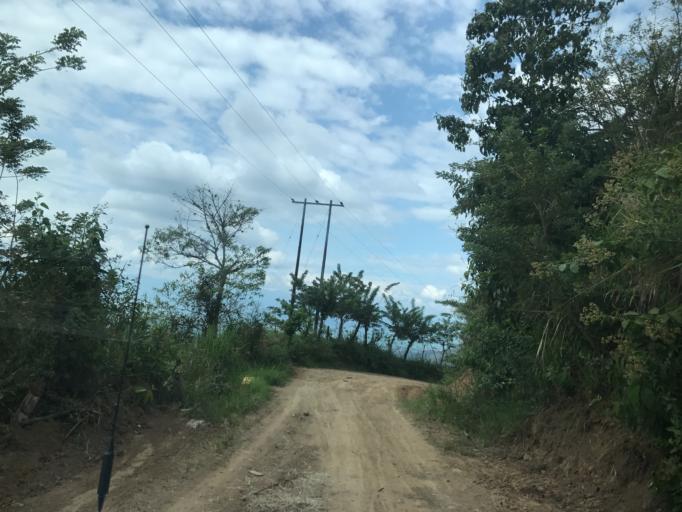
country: CO
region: Valle del Cauca
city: Obando
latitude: 4.5497
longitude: -75.9234
